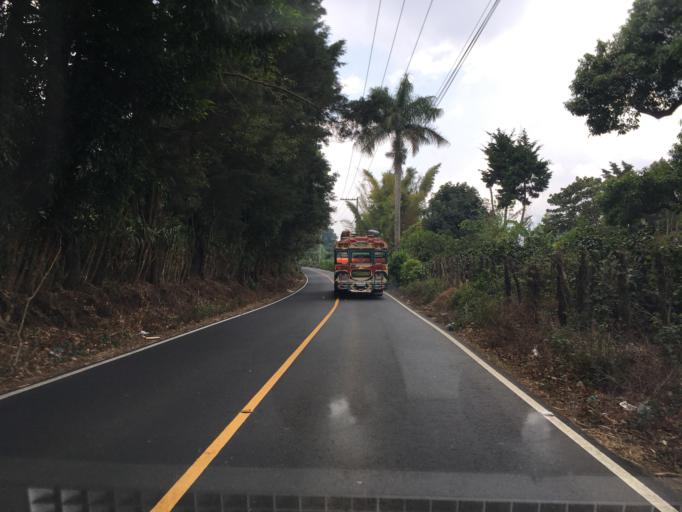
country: GT
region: Guatemala
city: Villa Canales
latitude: 14.4275
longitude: -90.5199
